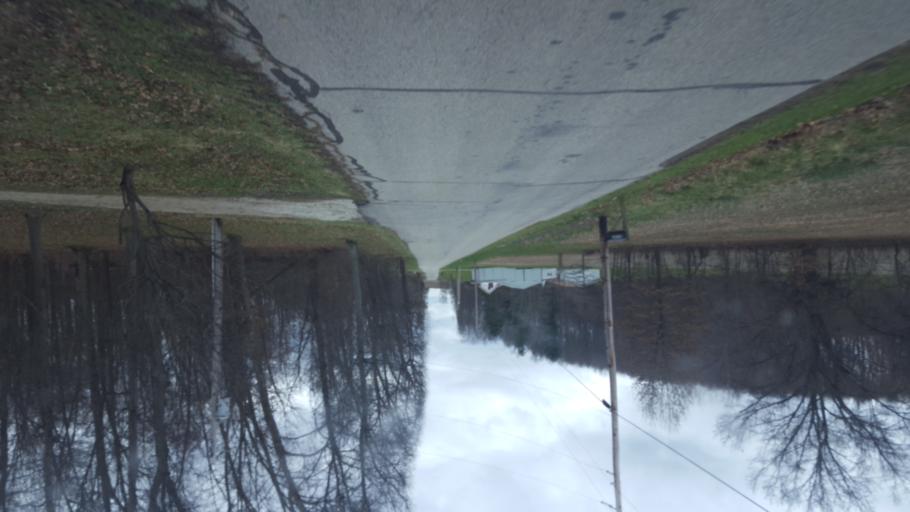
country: US
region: Ohio
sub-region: Licking County
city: Utica
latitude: 40.2005
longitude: -82.3914
